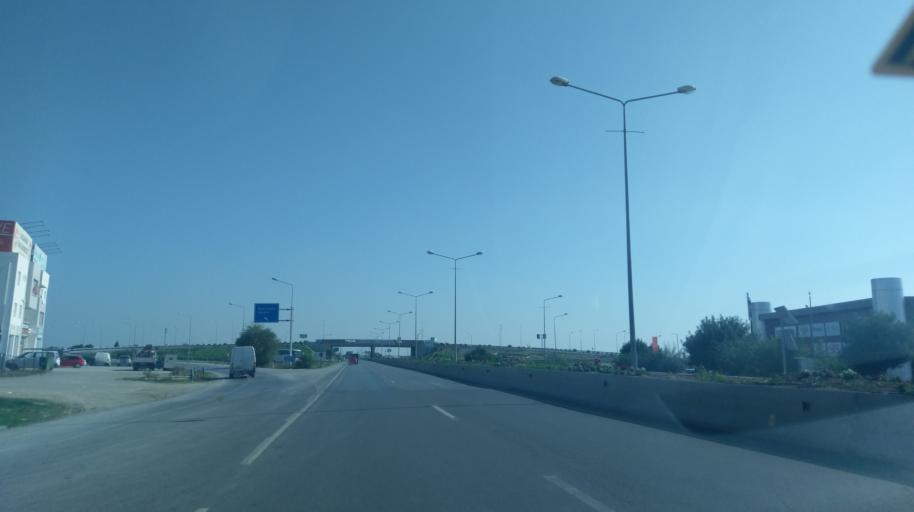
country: CY
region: Lefkosia
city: Geri
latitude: 35.2197
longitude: 33.4945
